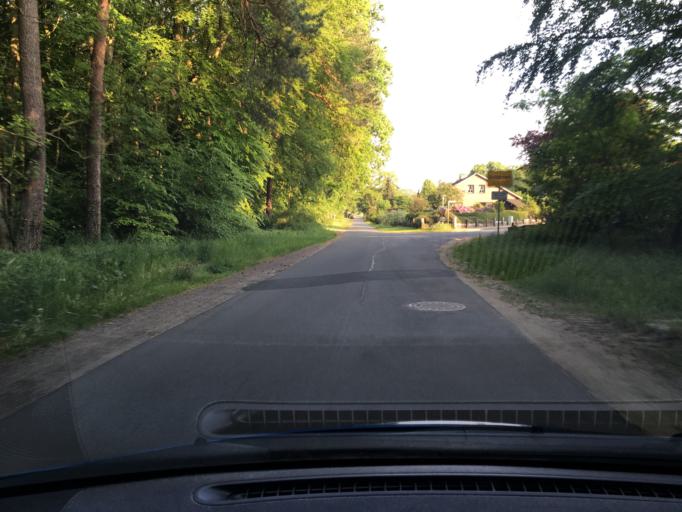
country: DE
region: Lower Saxony
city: Rullstorf
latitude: 53.2811
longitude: 10.5669
